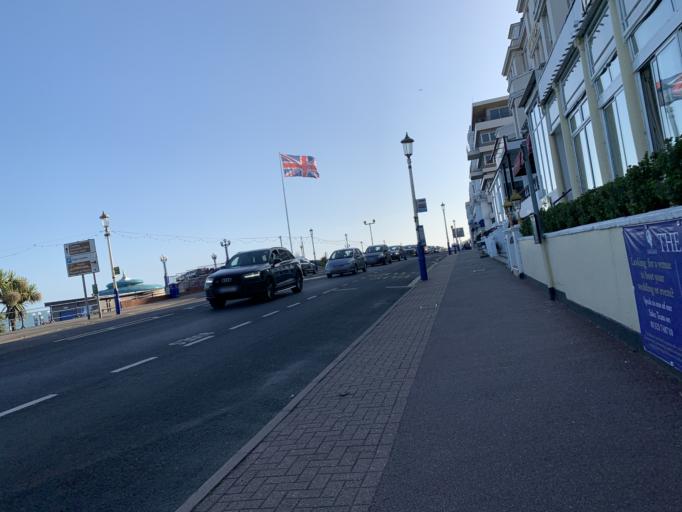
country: GB
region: England
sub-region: East Sussex
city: Eastbourne
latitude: 50.7652
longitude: 0.2896
